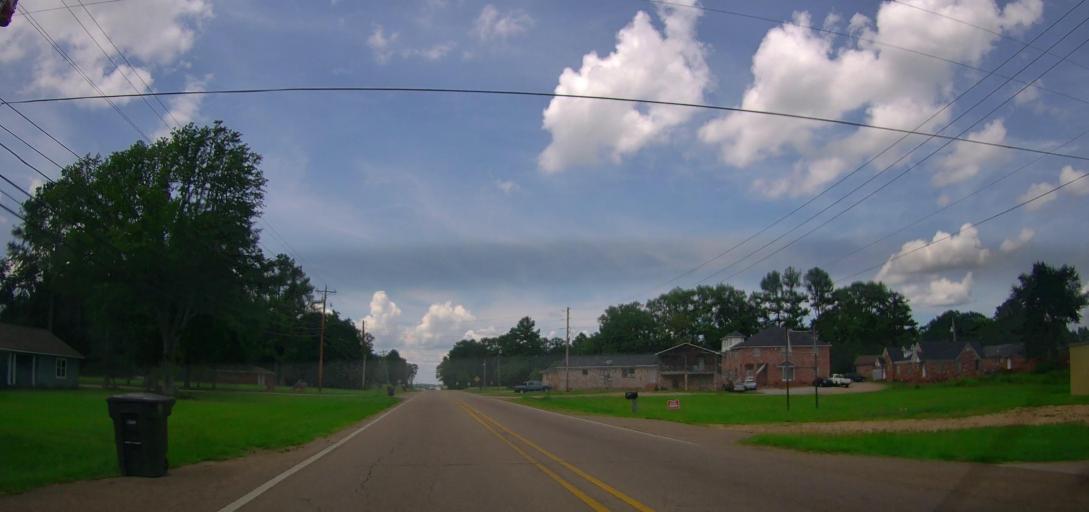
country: US
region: Mississippi
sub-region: Lee County
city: Shannon
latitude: 34.1291
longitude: -88.7193
